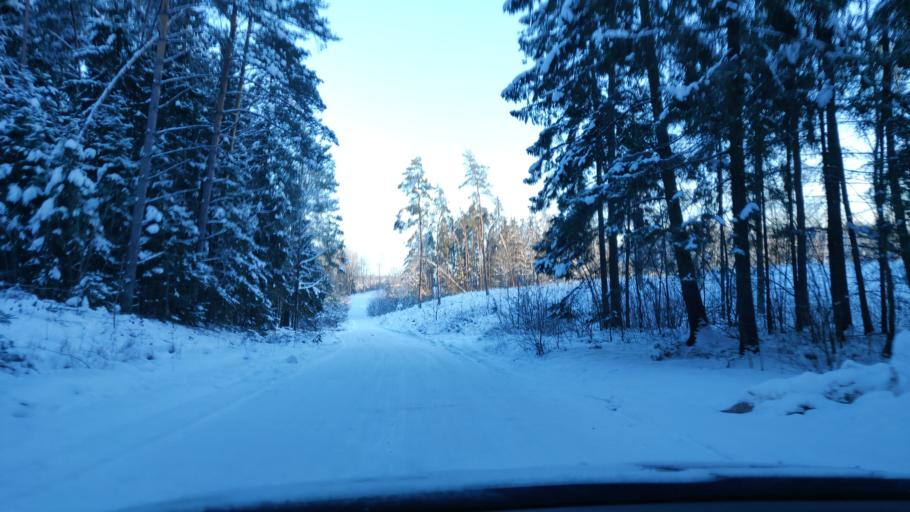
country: LT
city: Trakai
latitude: 54.6138
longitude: 24.9299
